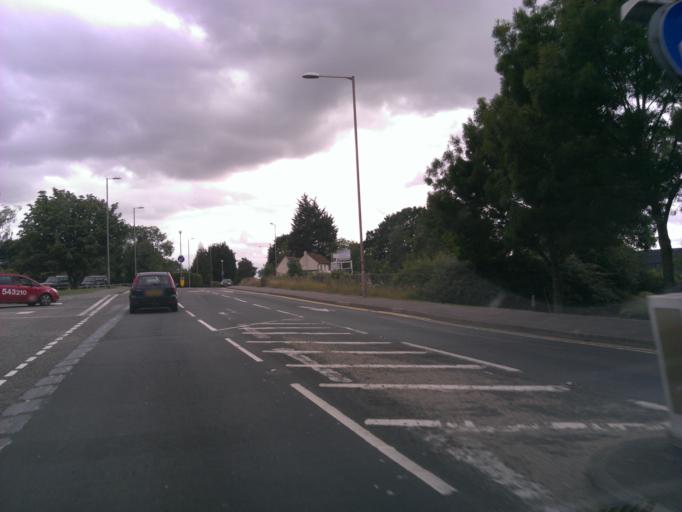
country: GB
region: England
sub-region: Essex
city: Colchester
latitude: 51.9196
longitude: 0.9330
